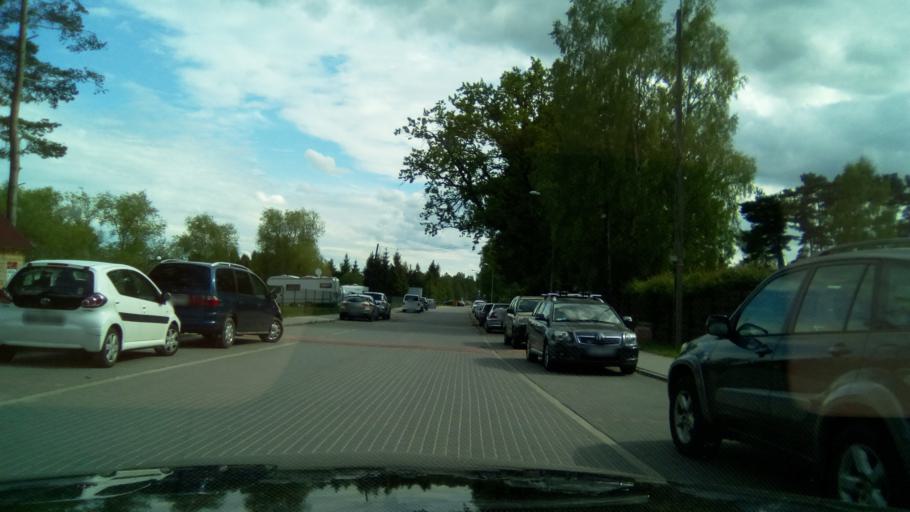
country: PL
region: Pomeranian Voivodeship
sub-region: Powiat pucki
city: Wierzchucino
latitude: 54.8286
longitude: 18.0763
